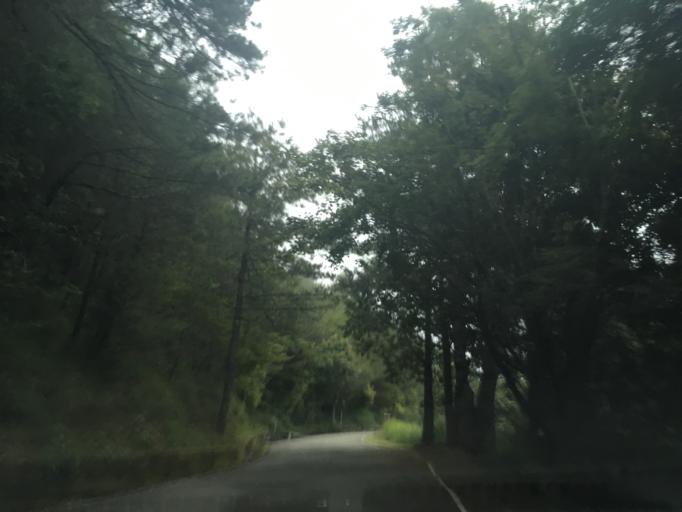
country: TW
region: Taiwan
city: Fengyuan
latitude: 24.2818
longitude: 121.0283
